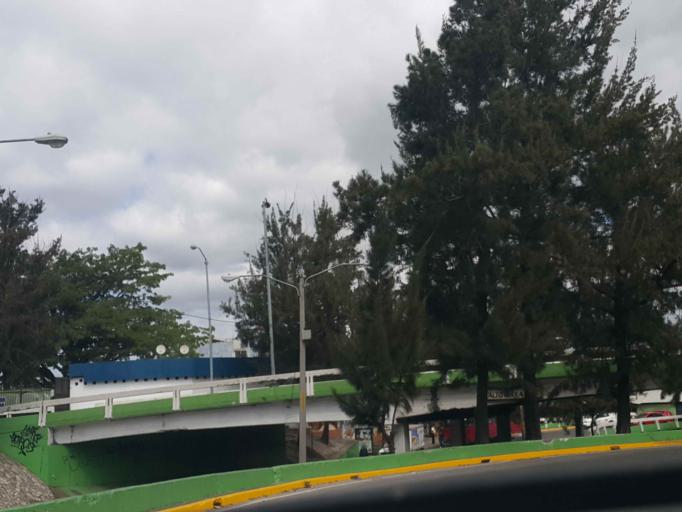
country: GT
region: Guatemala
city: Guatemala City
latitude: 14.6296
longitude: -90.5175
